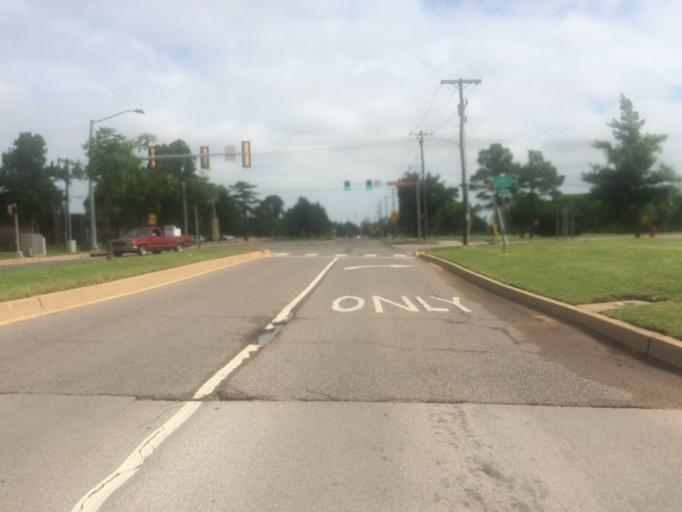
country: US
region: Oklahoma
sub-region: Cleveland County
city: Norman
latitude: 35.1908
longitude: -97.4412
